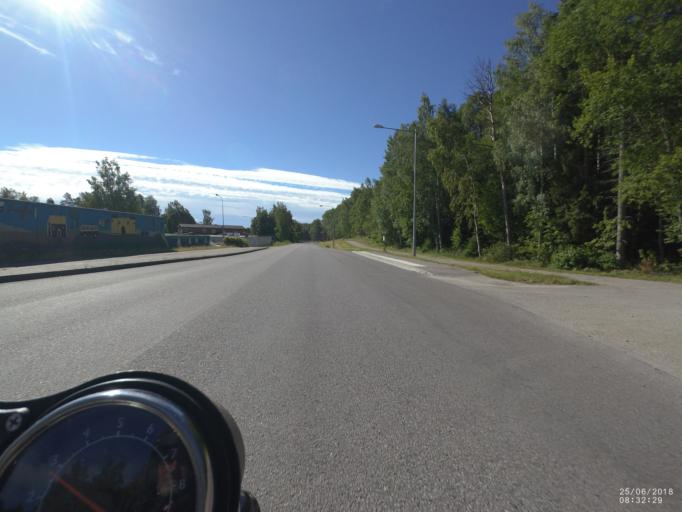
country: SE
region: Soedermanland
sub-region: Nykopings Kommun
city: Nykoping
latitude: 58.7315
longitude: 17.0265
